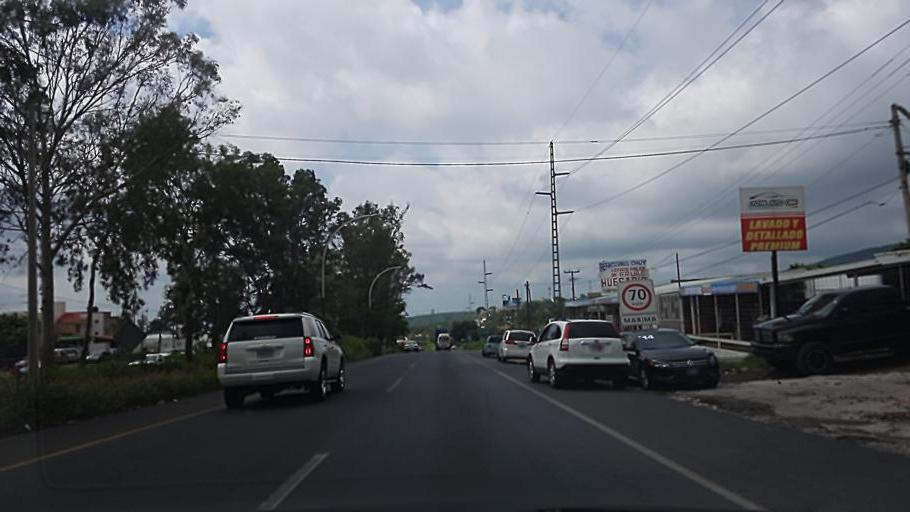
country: MX
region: Nayarit
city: Tepic
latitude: 21.5174
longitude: -104.9249
